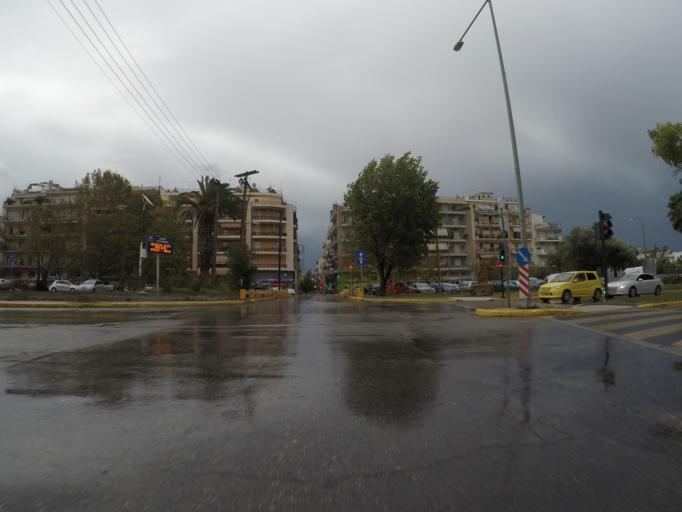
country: GR
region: Peloponnese
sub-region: Nomos Messinias
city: Kalamata
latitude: 37.0397
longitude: 22.1079
